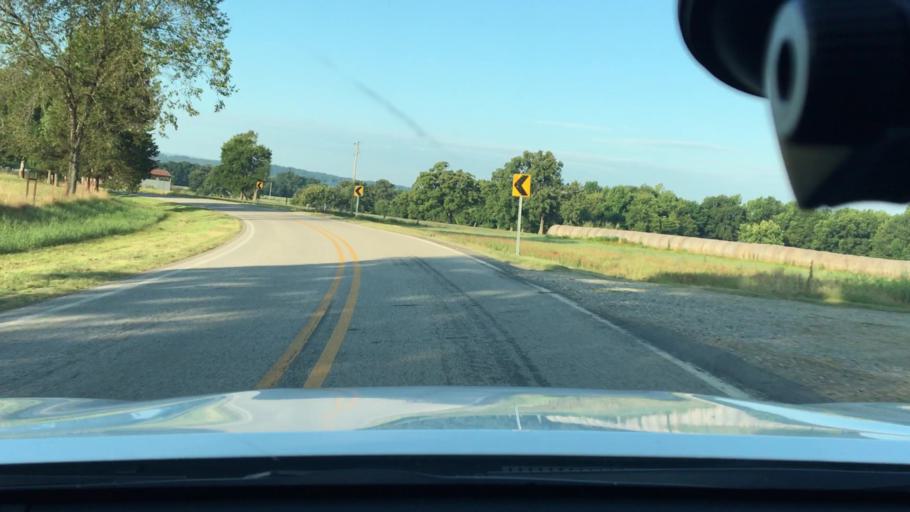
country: US
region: Arkansas
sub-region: Johnson County
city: Coal Hill
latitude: 35.3549
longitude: -93.5659
